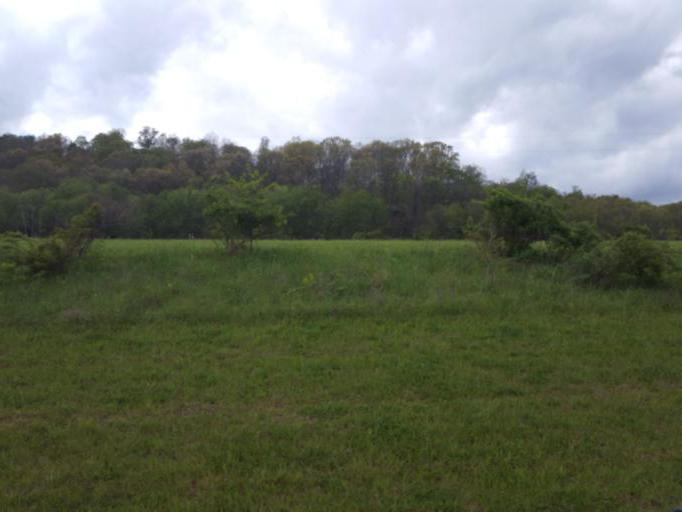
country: US
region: Ohio
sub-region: Ashland County
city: Loudonville
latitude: 40.5495
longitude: -82.2023
